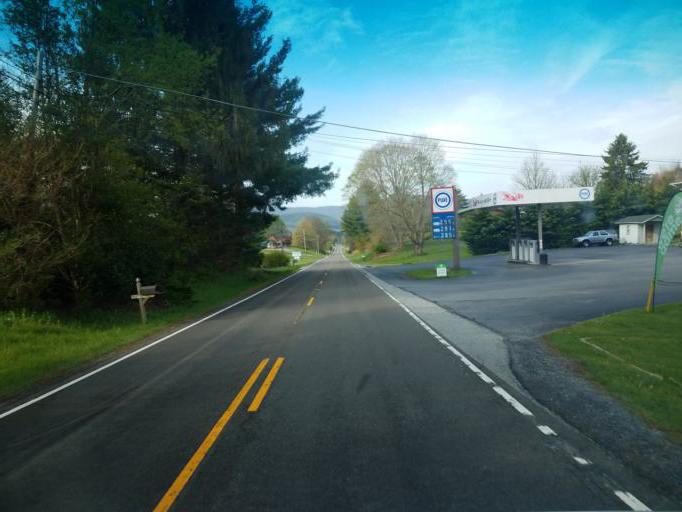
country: US
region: Virginia
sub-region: Smyth County
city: Atkins
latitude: 36.7879
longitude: -81.4031
